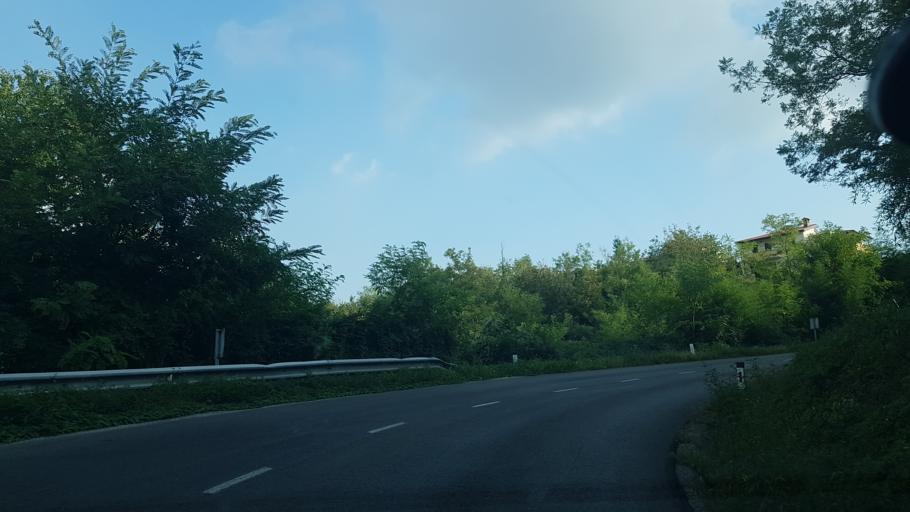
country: SI
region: Nova Gorica
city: Nova Gorica
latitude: 45.9480
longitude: 13.6442
